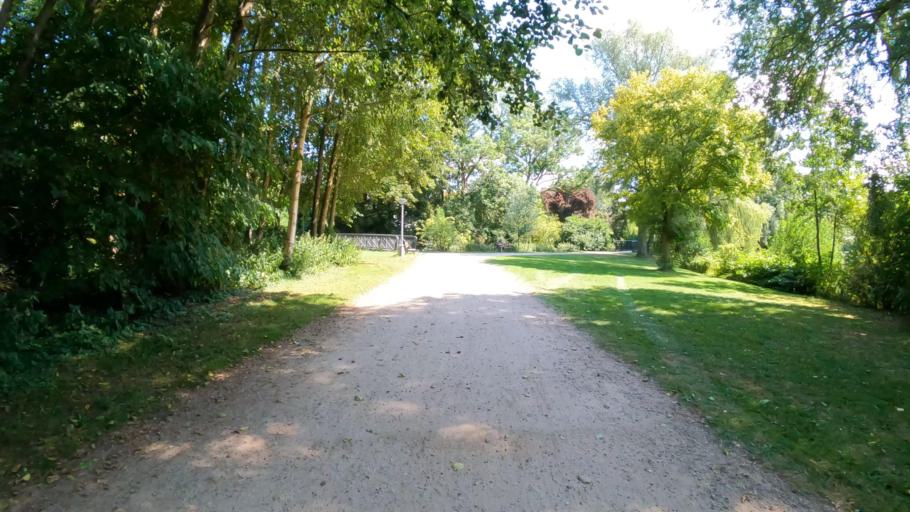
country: DE
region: Schleswig-Holstein
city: Elmshorn
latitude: 53.7543
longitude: 9.6637
